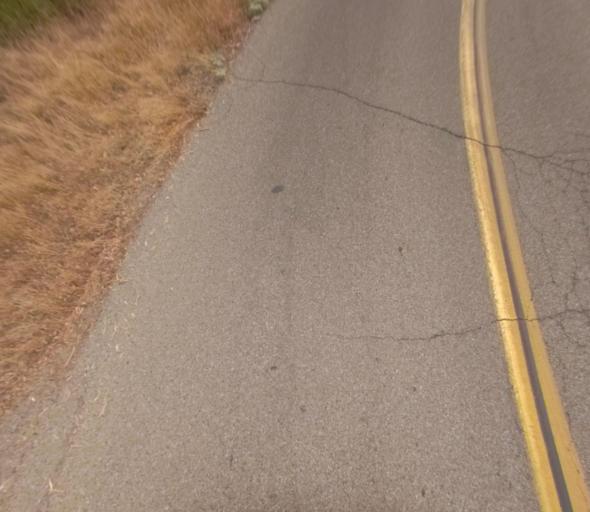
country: US
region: California
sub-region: Madera County
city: Oakhurst
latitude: 37.3320
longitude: -119.6149
